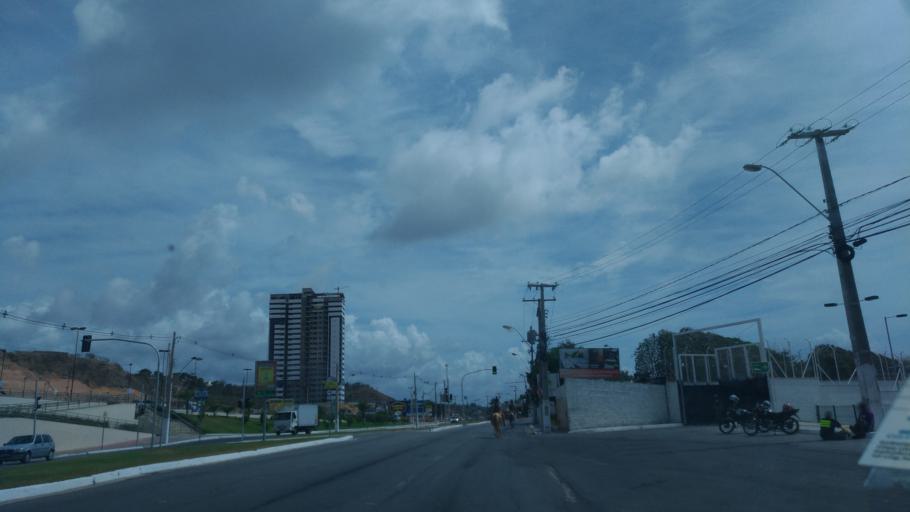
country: BR
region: Alagoas
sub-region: Maceio
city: Maceio
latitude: -9.6276
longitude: -35.6979
